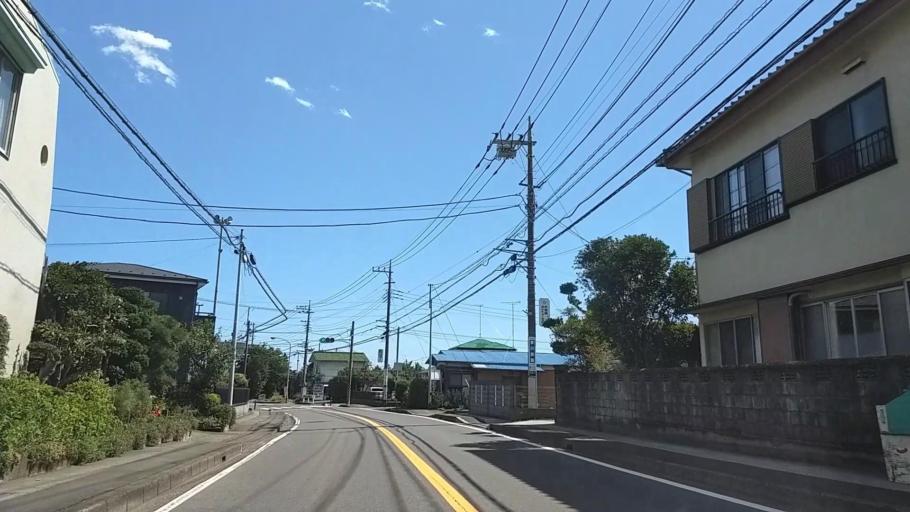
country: JP
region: Kanagawa
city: Zama
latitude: 35.5364
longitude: 139.3080
